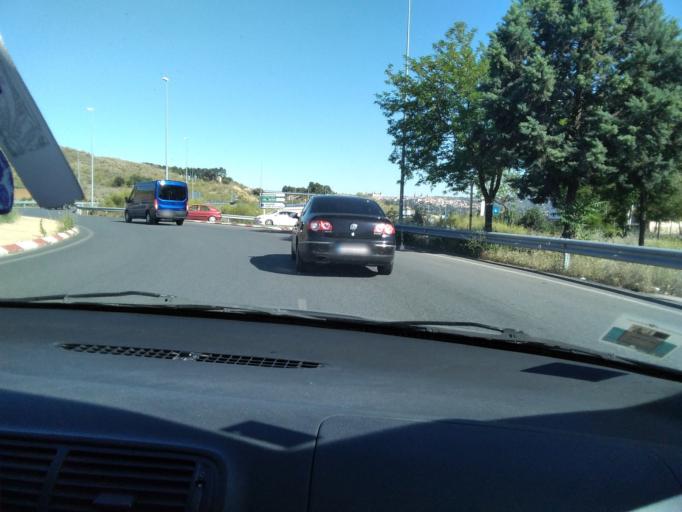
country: ES
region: Castille-La Mancha
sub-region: Province of Toledo
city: Toledo
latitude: 39.8855
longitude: -4.0555
